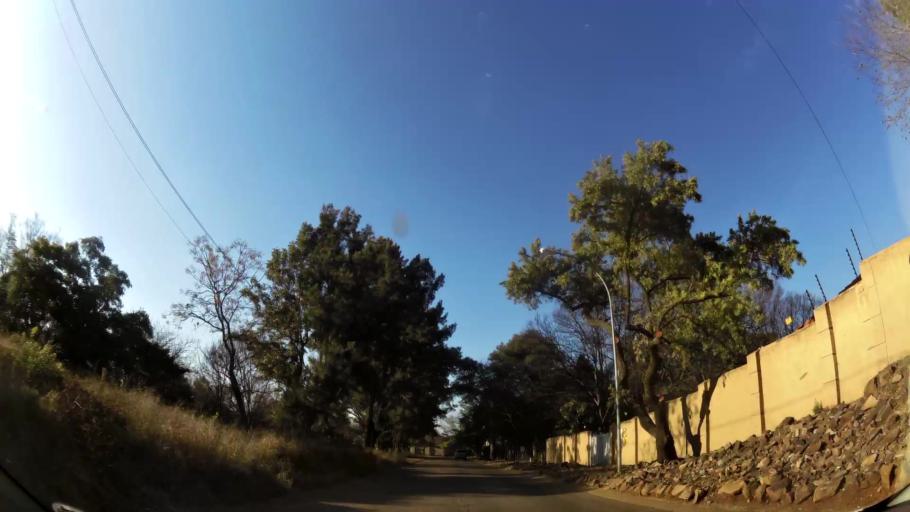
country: ZA
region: Gauteng
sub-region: City of Tshwane Metropolitan Municipality
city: Centurion
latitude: -25.8662
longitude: 28.1382
